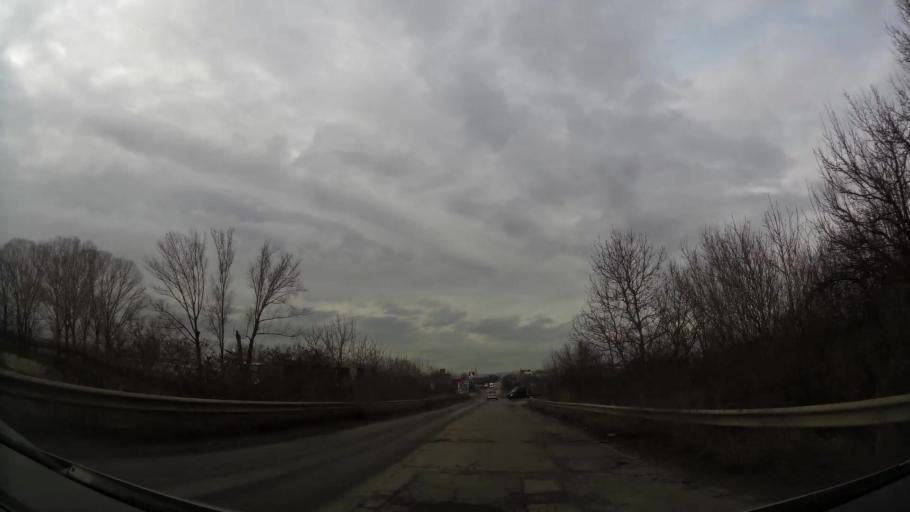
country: BG
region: Sofia-Capital
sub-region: Stolichna Obshtina
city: Sofia
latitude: 42.7507
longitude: 23.2756
